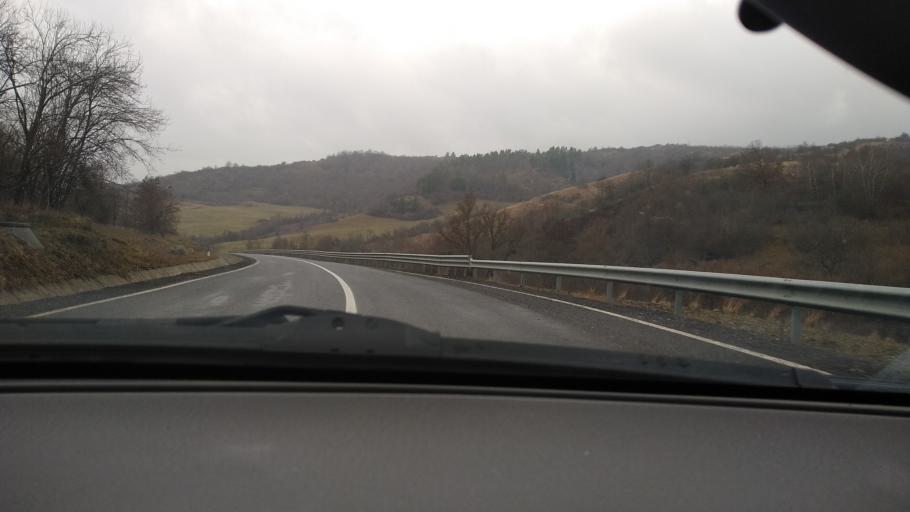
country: RO
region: Mures
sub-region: Comuna Magherani
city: Magherani
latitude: 46.5823
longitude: 24.9430
